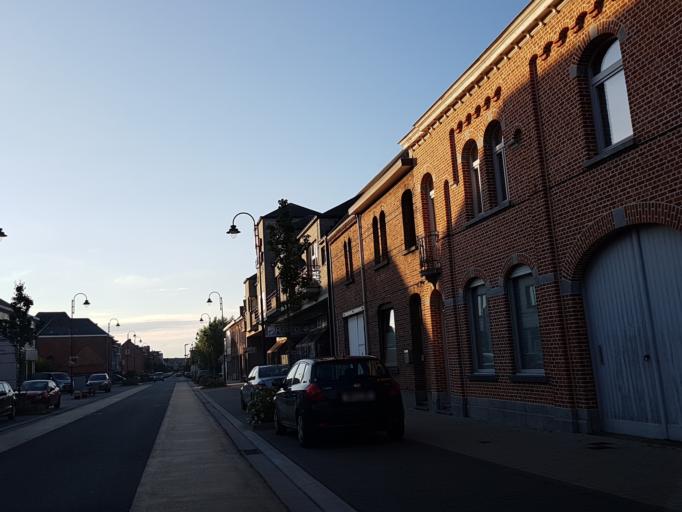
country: BE
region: Flanders
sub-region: Provincie Oost-Vlaanderen
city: Lebbeke
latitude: 50.9940
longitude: 4.1324
